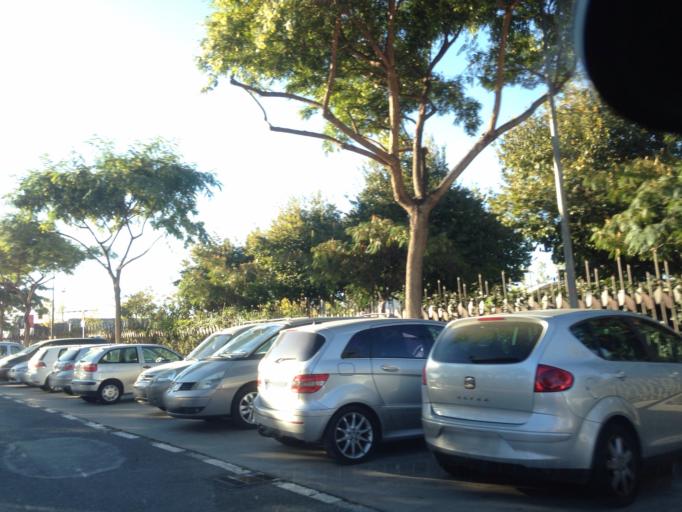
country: ES
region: Andalusia
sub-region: Provincia de Malaga
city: Malaga
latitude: 36.7544
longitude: -4.4247
